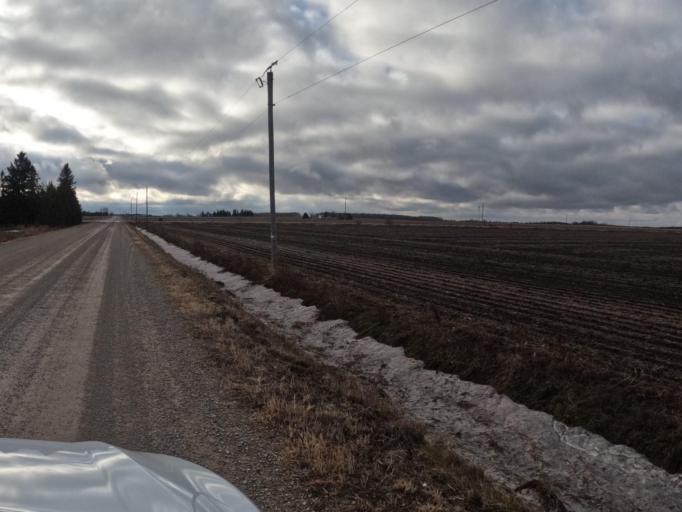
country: CA
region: Ontario
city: Shelburne
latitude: 43.8914
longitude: -80.3604
